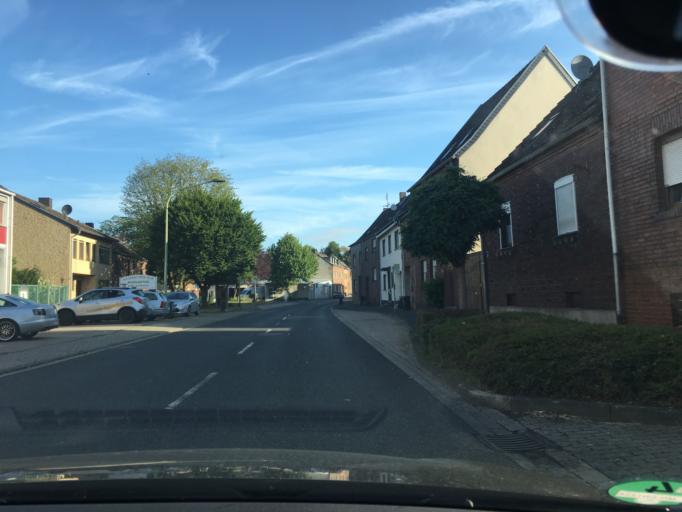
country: DE
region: North Rhine-Westphalia
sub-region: Regierungsbezirk Koln
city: Niederzier
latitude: 50.9007
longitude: 6.4449
